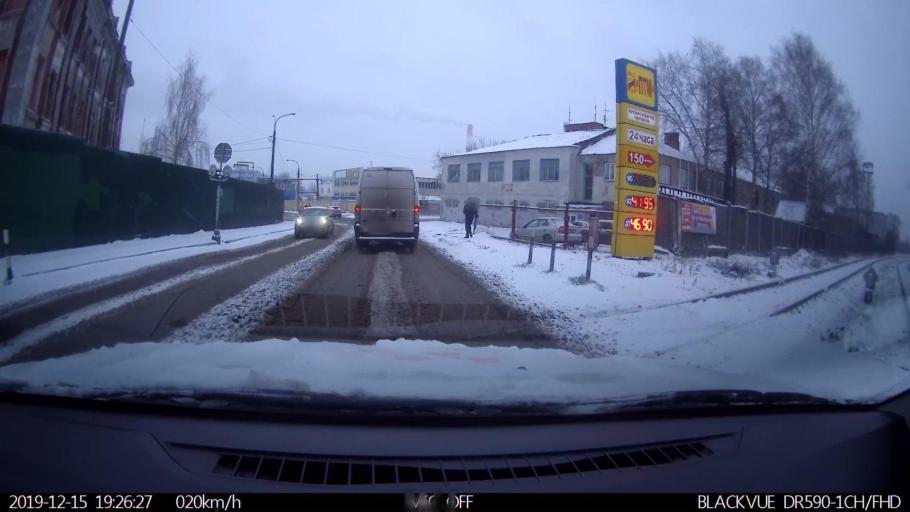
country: RU
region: Nizjnij Novgorod
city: Neklyudovo
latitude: 56.3510
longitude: 43.8756
